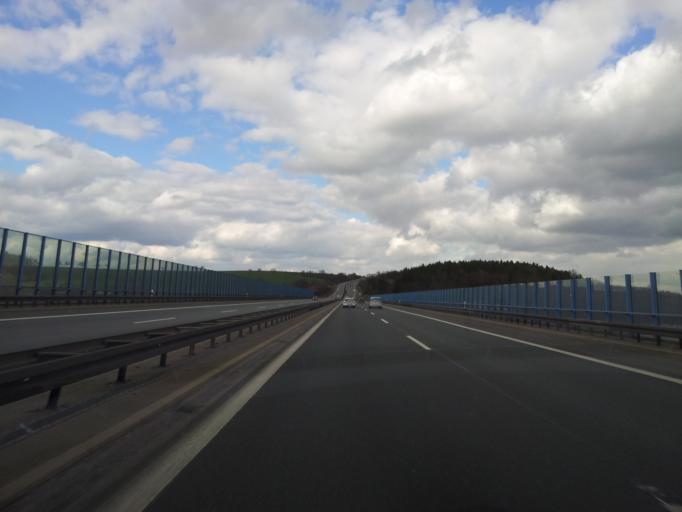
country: DE
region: Saxony
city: Neuensalz
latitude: 50.5159
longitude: 12.2266
